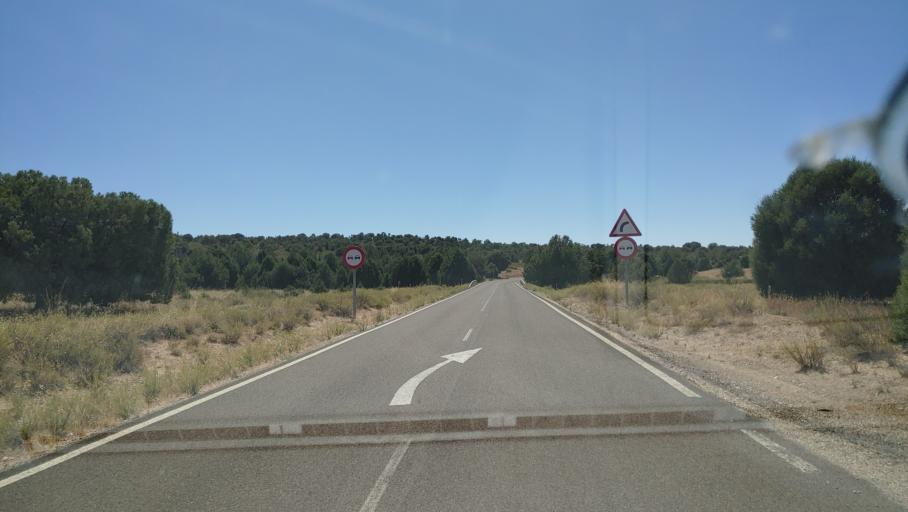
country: ES
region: Castille-La Mancha
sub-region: Provincia de Albacete
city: Ossa de Montiel
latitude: 38.8716
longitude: -2.7880
